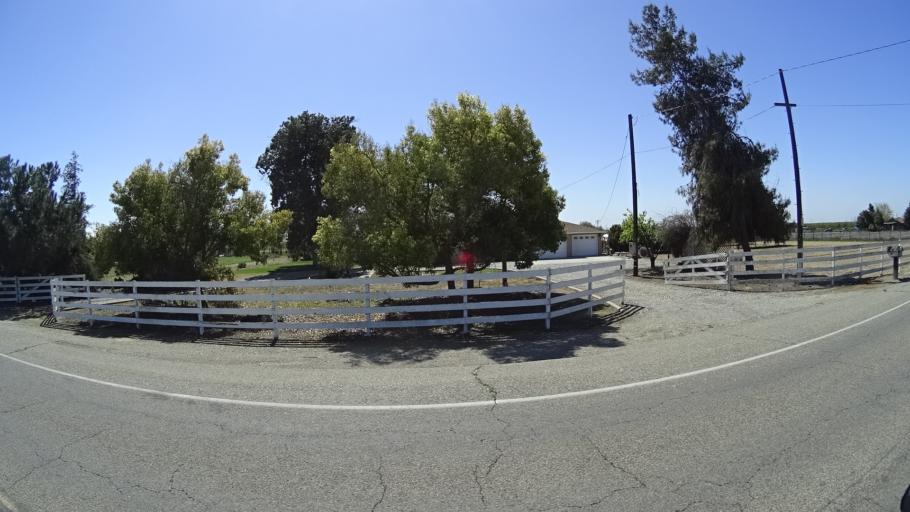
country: US
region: California
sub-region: Fresno County
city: West Park
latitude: 36.7064
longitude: -119.8646
